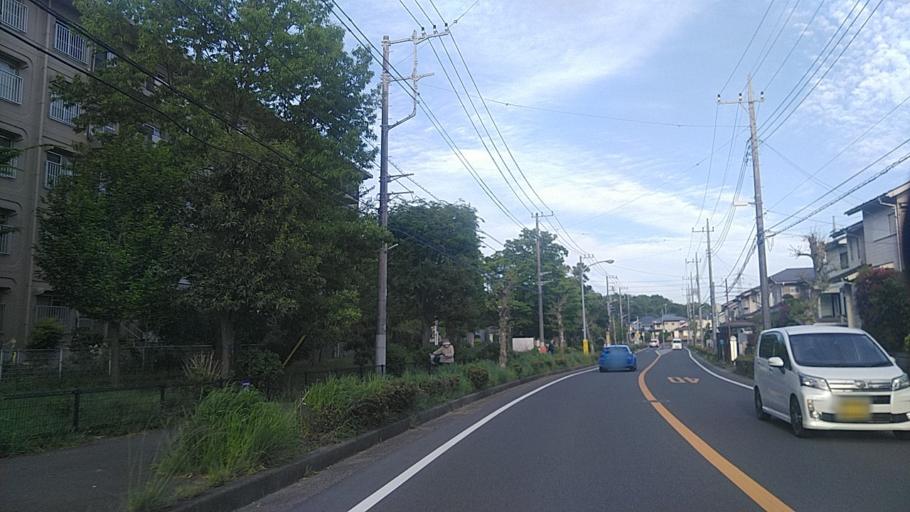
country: JP
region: Chiba
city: Shiroi
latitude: 35.7937
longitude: 140.1398
